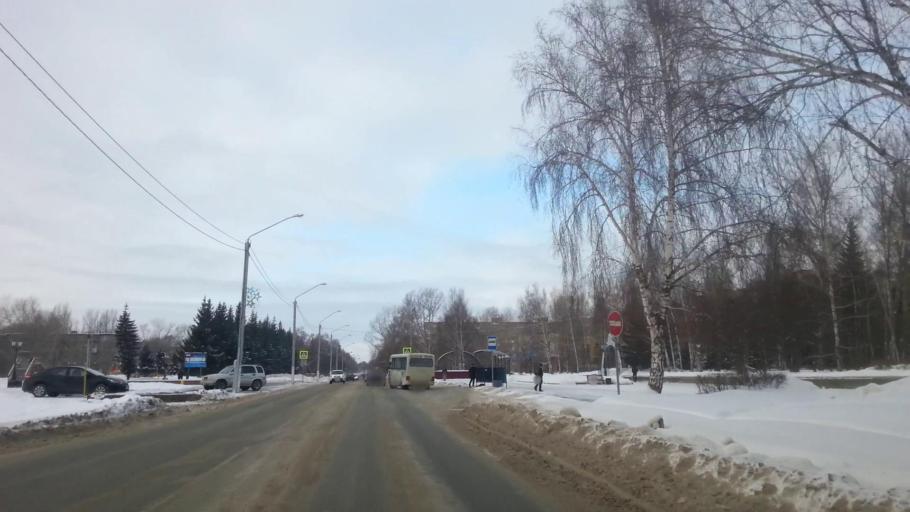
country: RU
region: Altai Krai
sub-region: Gorod Barnaulskiy
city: Barnaul
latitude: 53.3654
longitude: 83.6917
